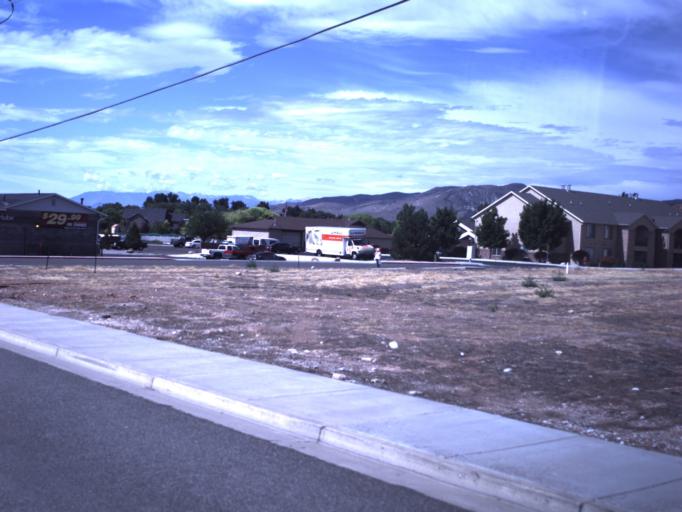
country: US
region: Utah
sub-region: Sevier County
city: Richfield
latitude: 38.7825
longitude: -112.0849
